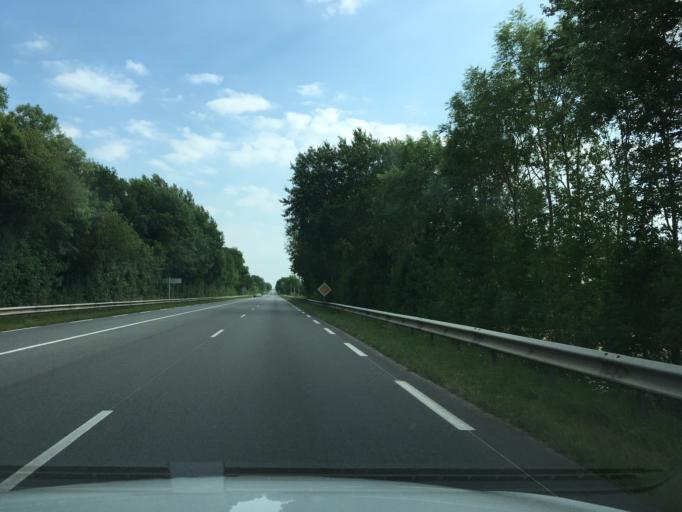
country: FR
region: Poitou-Charentes
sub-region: Departement des Deux-Sevres
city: Le Tallud
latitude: 46.6117
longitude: -0.2848
